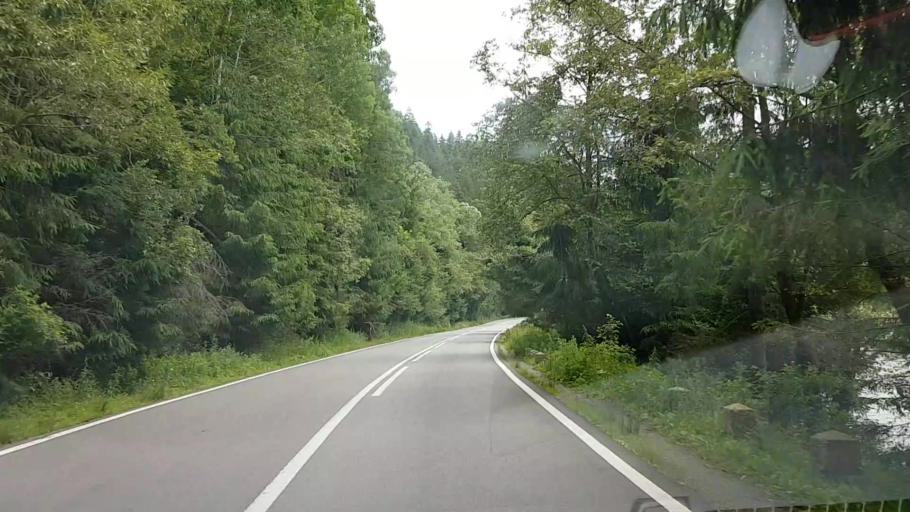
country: RO
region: Suceava
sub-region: Comuna Crucea
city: Crucea
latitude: 47.3629
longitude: 25.6007
